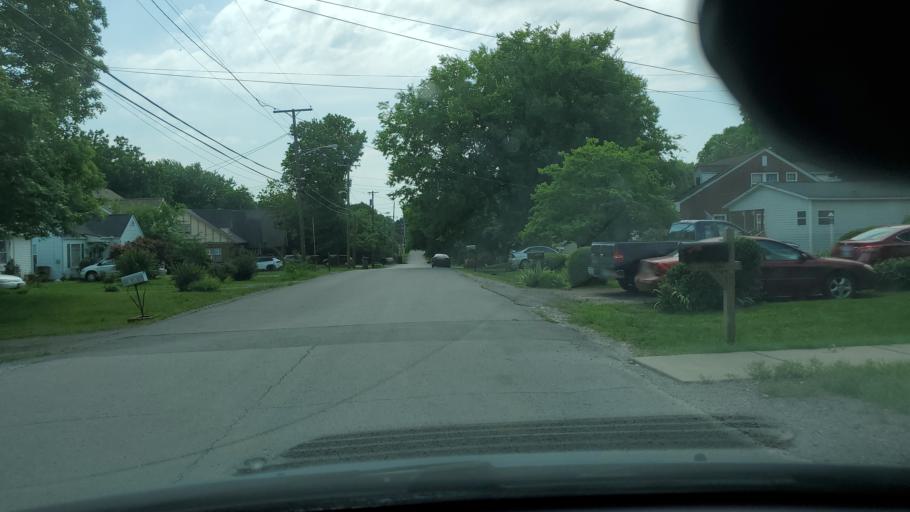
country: US
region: Tennessee
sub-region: Davidson County
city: Nashville
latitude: 36.2305
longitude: -86.7294
